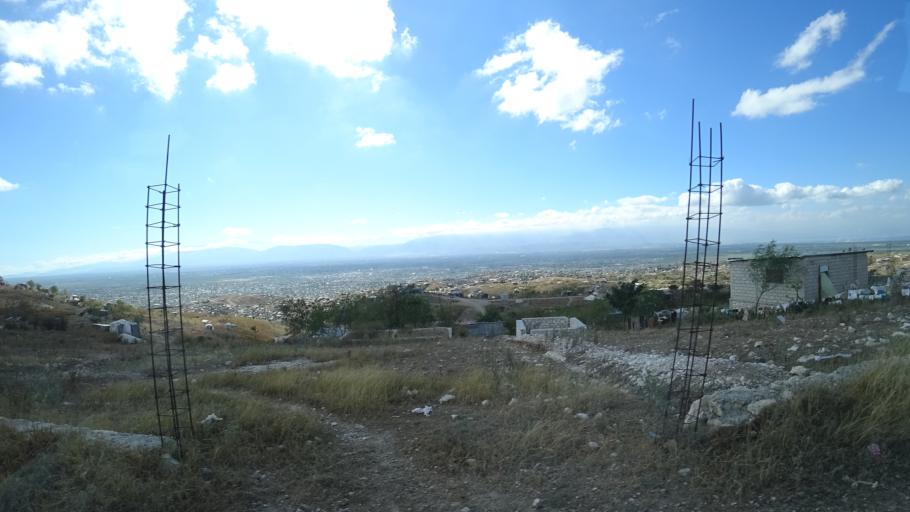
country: HT
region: Ouest
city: Croix des Bouquets
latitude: 18.6724
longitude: -72.2696
